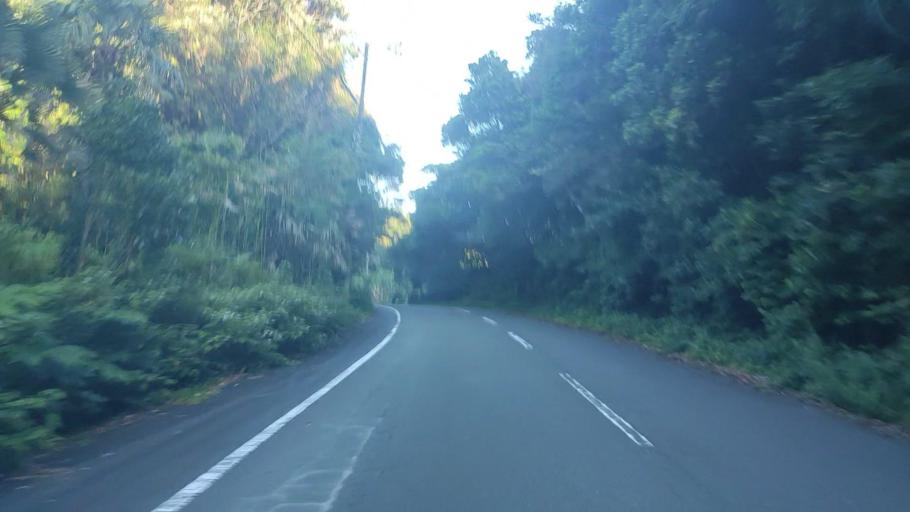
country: JP
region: Mie
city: Ise
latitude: 34.2669
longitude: 136.7697
